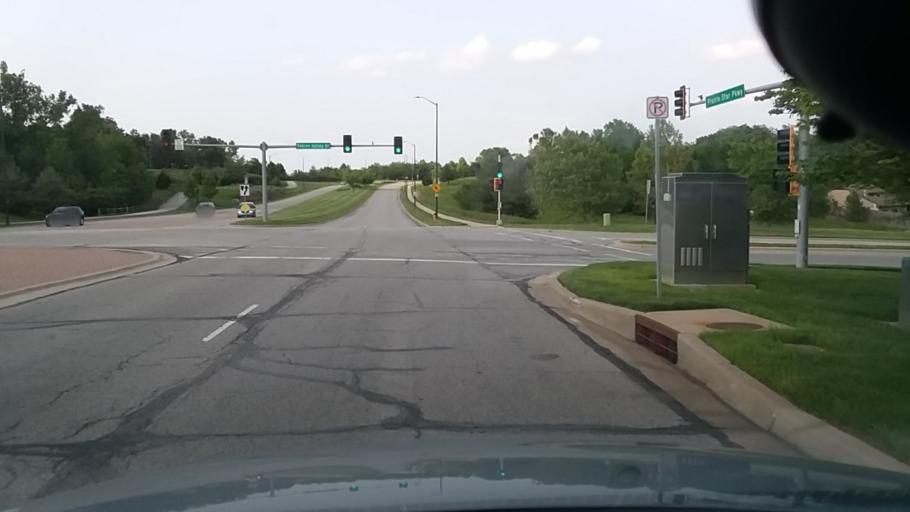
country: US
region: Kansas
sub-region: Johnson County
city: Olathe
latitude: 38.9523
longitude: -94.8110
